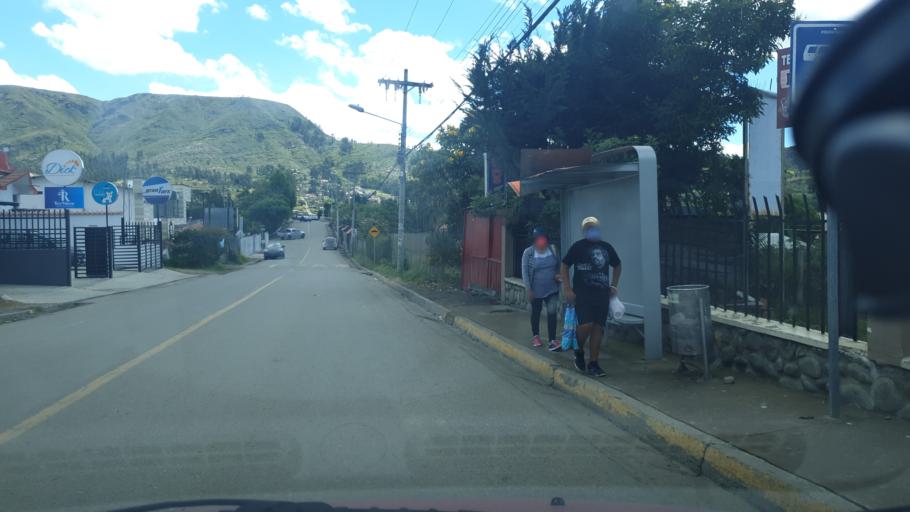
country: EC
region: Azuay
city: Llacao
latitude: -2.8551
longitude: -78.9101
